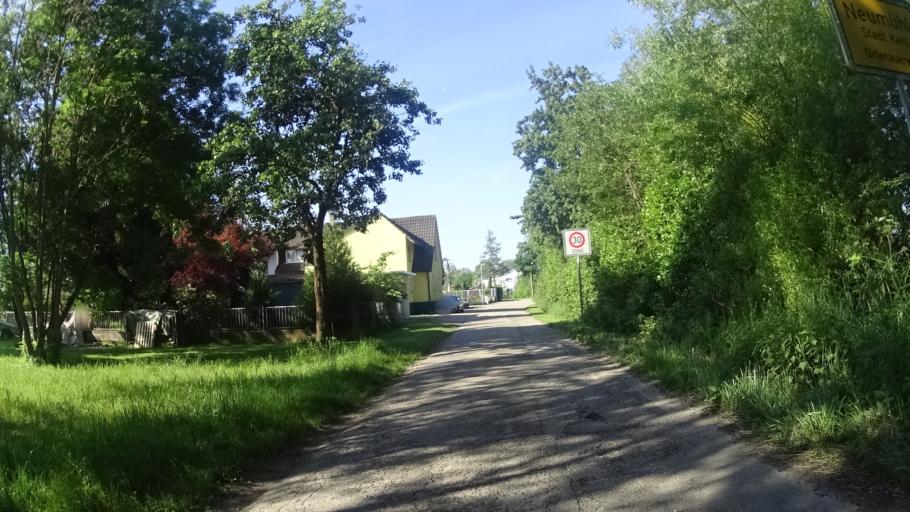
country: DE
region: Baden-Wuerttemberg
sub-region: Freiburg Region
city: Kehl
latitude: 48.5700
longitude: 7.8521
